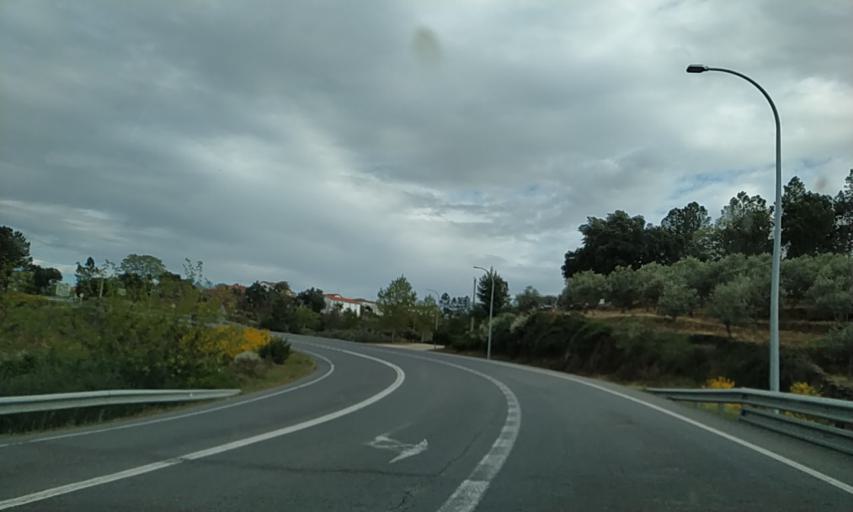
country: ES
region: Extremadura
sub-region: Provincia de Caceres
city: Perales del Puerto
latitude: 40.1623
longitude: -6.6861
